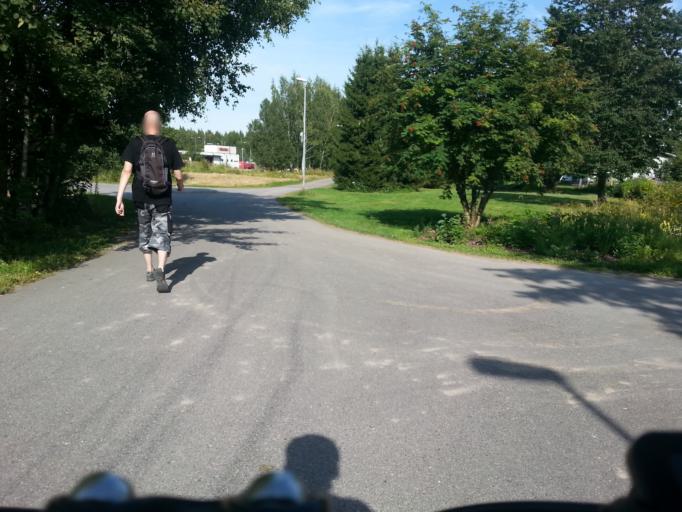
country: FI
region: Uusimaa
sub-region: Helsinki
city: Vantaa
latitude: 60.2398
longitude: 24.9963
